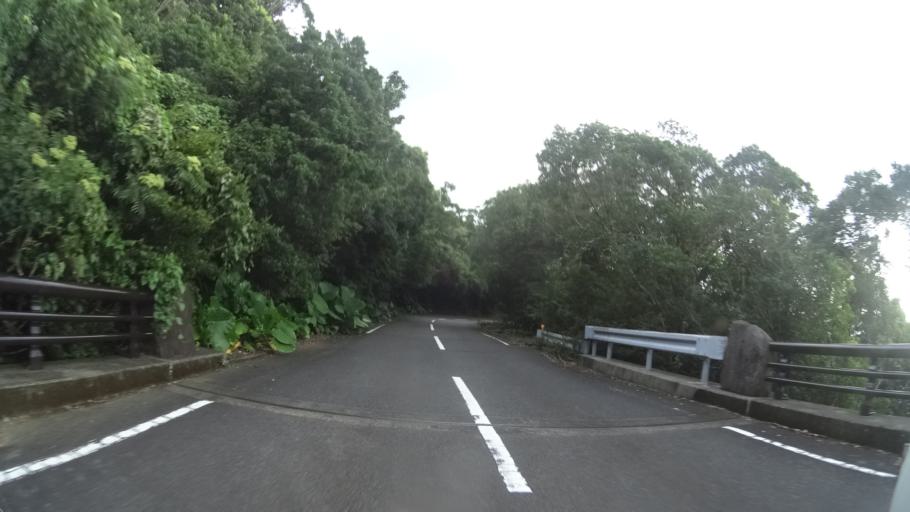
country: JP
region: Kagoshima
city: Nishinoomote
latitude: 30.3231
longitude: 130.3951
